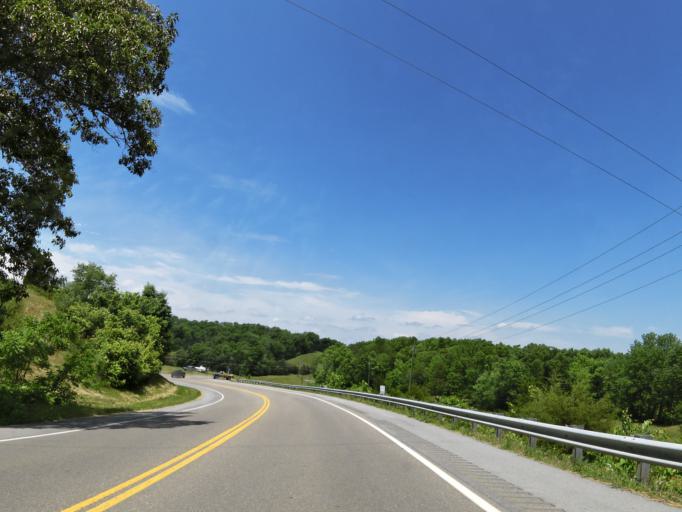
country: US
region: Tennessee
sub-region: Jefferson County
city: Dandridge
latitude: 35.9098
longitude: -83.4045
